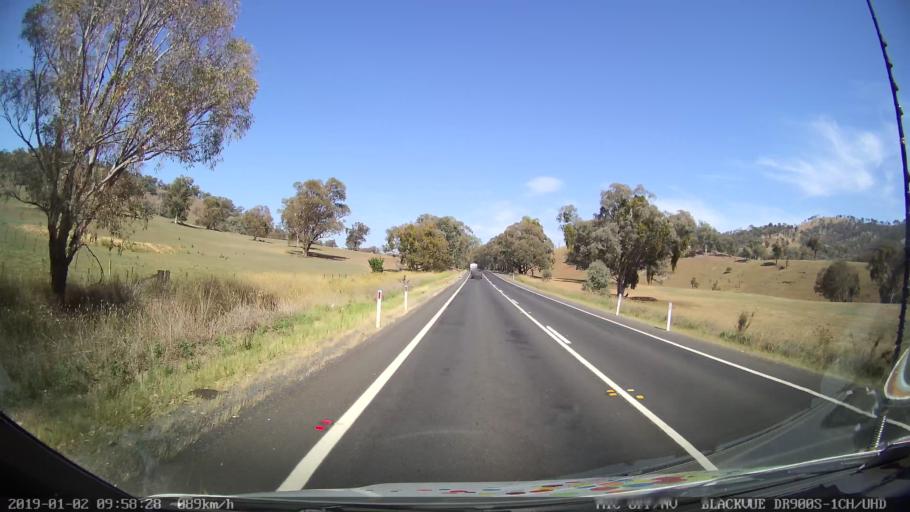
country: AU
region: New South Wales
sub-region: Tumut Shire
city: Tumut
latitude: -35.1971
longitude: 148.1567
